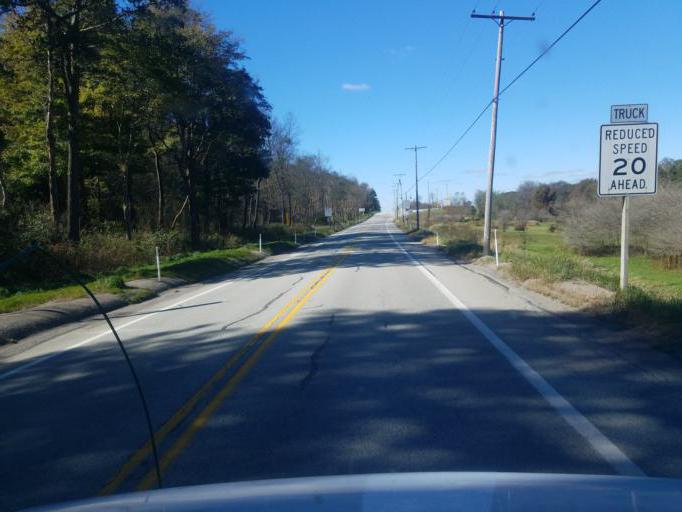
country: US
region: Pennsylvania
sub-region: Westmoreland County
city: Waterford
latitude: 40.1806
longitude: -79.1339
